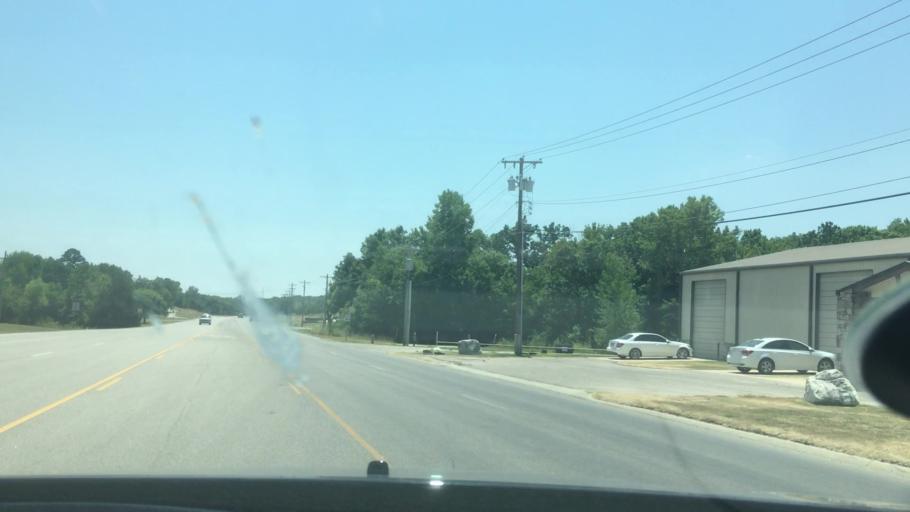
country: US
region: Oklahoma
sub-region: Pontotoc County
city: Ada
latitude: 34.7588
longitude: -96.6615
